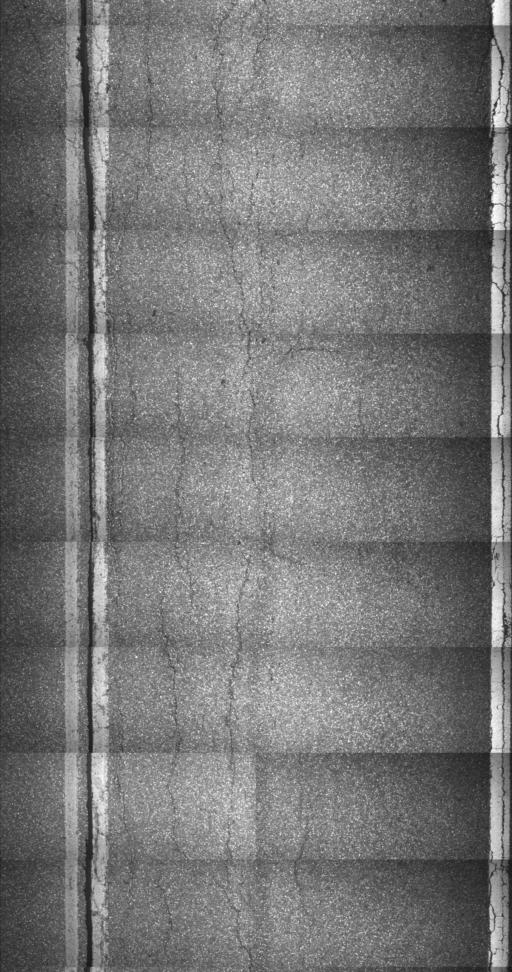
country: US
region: Vermont
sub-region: Addison County
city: Middlebury (village)
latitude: 43.9838
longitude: -73.1037
